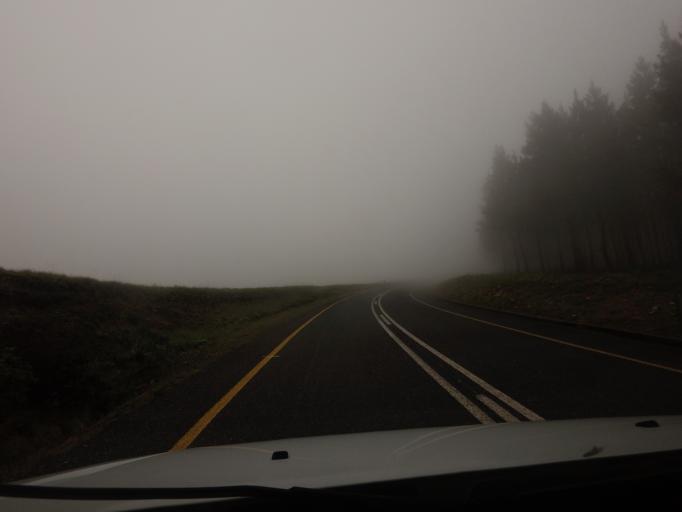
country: ZA
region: Mpumalanga
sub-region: Ehlanzeni District
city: Lydenburg
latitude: -25.1620
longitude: 30.6373
